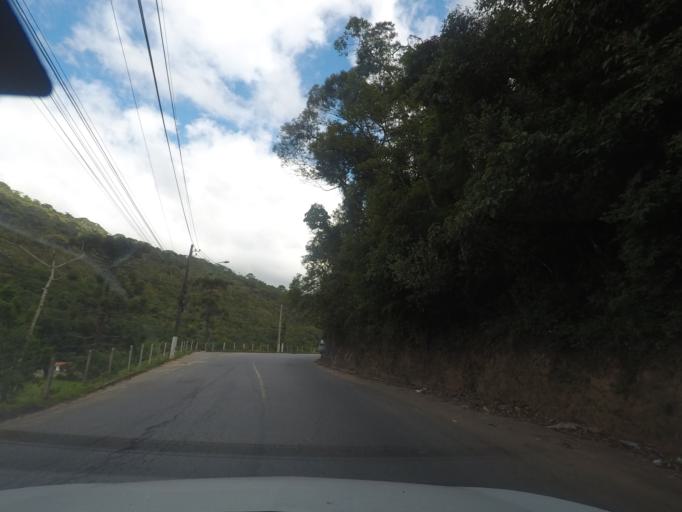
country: BR
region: Rio de Janeiro
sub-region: Teresopolis
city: Teresopolis
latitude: -22.3916
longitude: -42.9568
